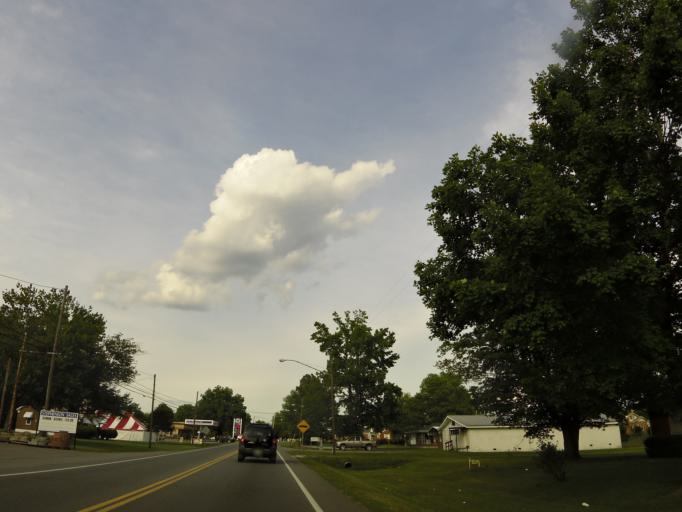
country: US
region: Tennessee
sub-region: Humphreys County
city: McEwen
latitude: 36.1076
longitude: -87.6396
